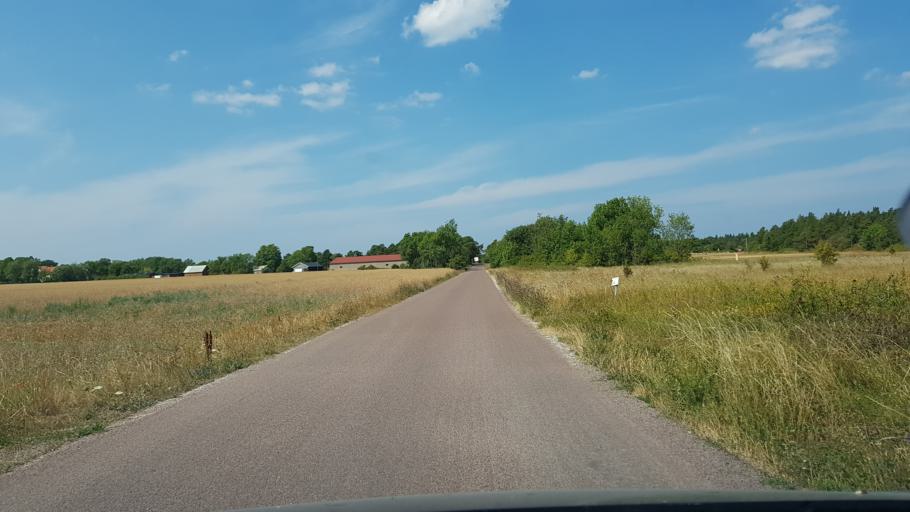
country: SE
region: Gotland
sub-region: Gotland
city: Visby
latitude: 57.6661
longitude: 18.3706
